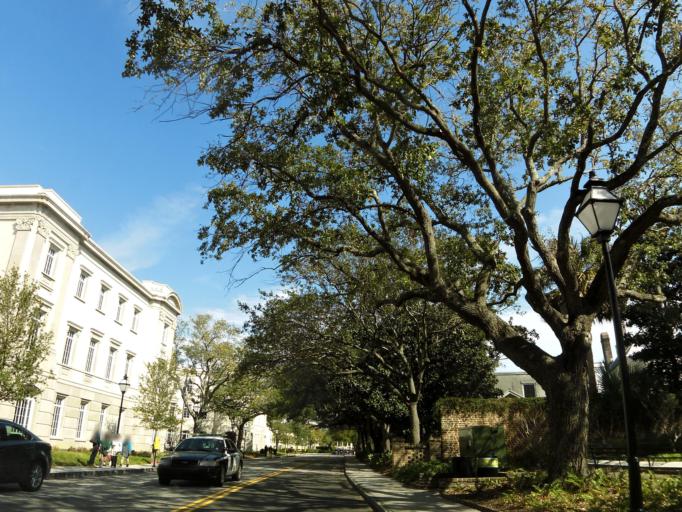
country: US
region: South Carolina
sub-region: Charleston County
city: Charleston
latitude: 32.7860
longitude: -79.9313
